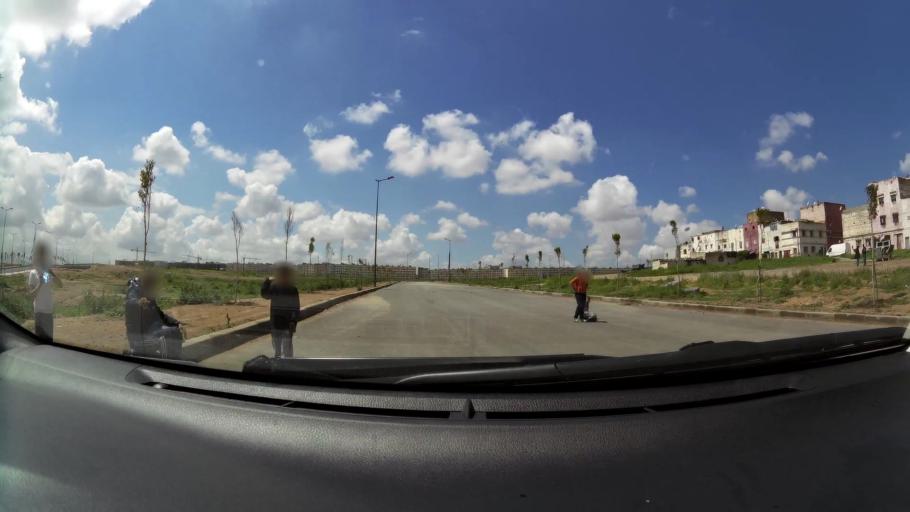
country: MA
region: Grand Casablanca
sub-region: Mediouna
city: Tit Mellil
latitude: 33.5430
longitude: -7.5459
